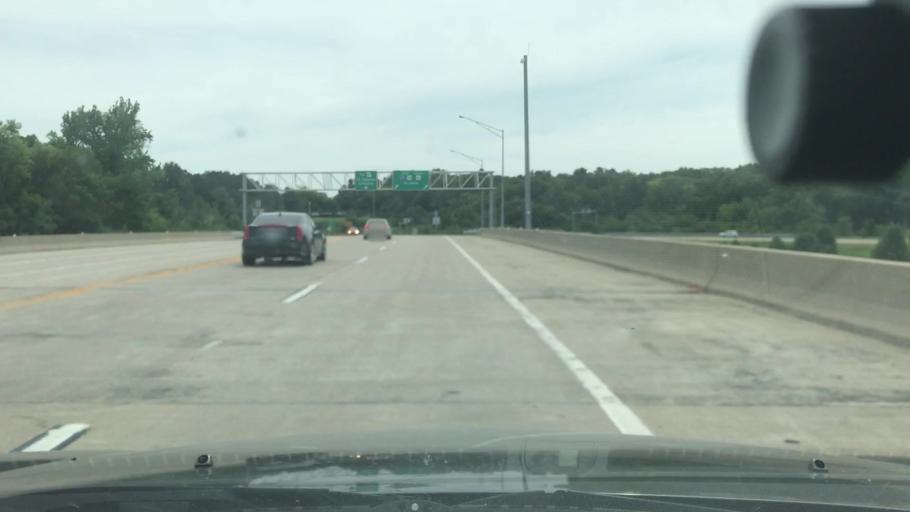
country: US
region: Missouri
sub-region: Saint Charles County
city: Weldon Spring
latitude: 38.7144
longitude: -90.7037
